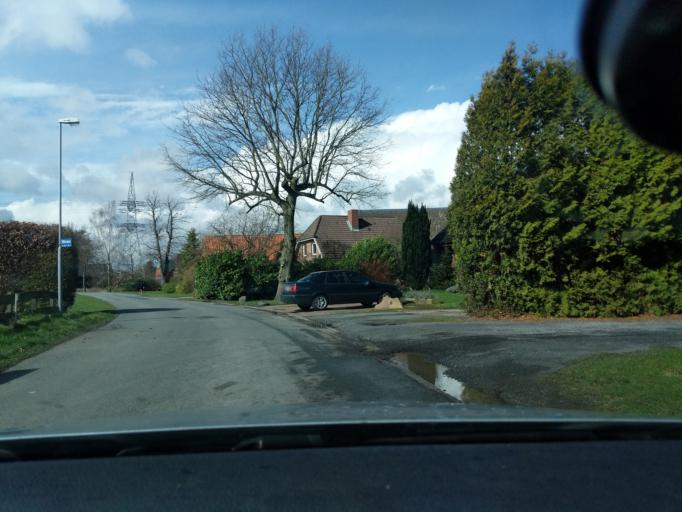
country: DE
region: Lower Saxony
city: Stade
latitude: 53.6092
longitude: 9.5166
